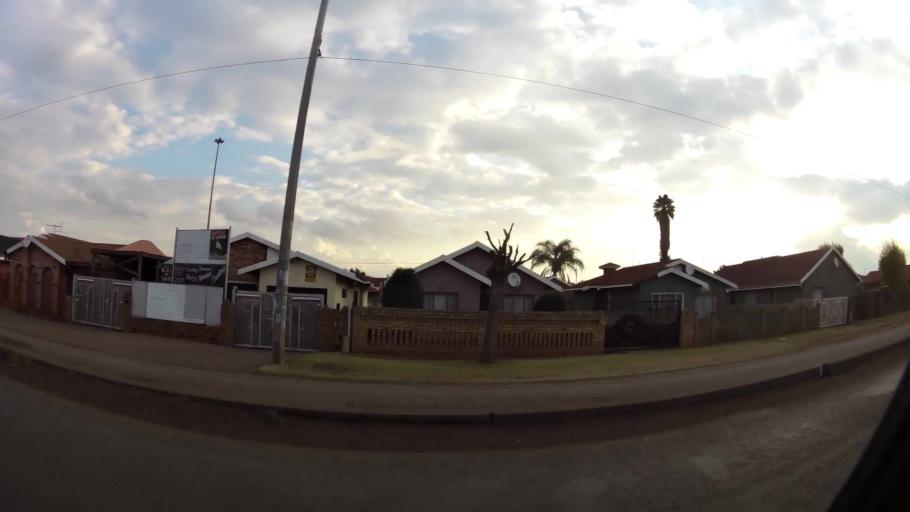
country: ZA
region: Gauteng
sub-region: City of Johannesburg Metropolitan Municipality
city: Orange Farm
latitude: -26.5862
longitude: 27.8453
